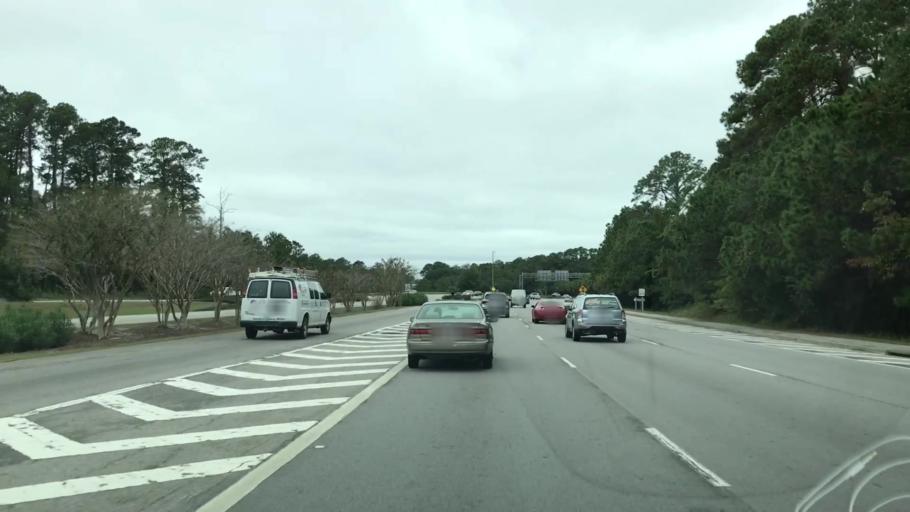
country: US
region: South Carolina
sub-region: Beaufort County
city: Hilton Head Island
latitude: 32.2158
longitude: -80.7431
